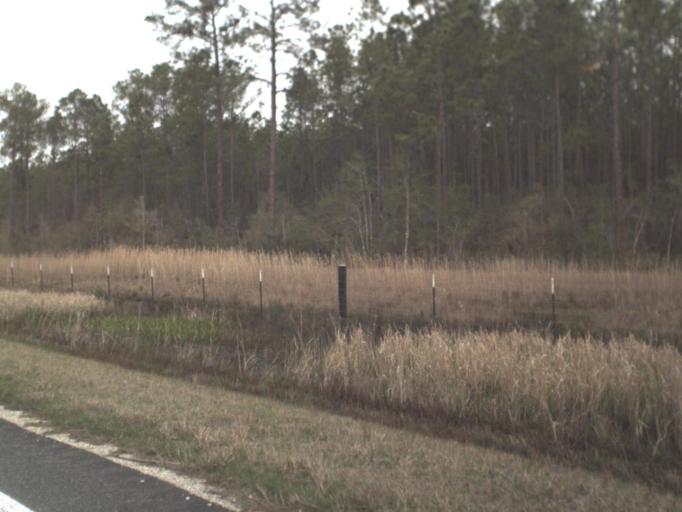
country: US
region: Florida
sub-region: Leon County
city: Woodville
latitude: 30.1976
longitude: -84.1573
